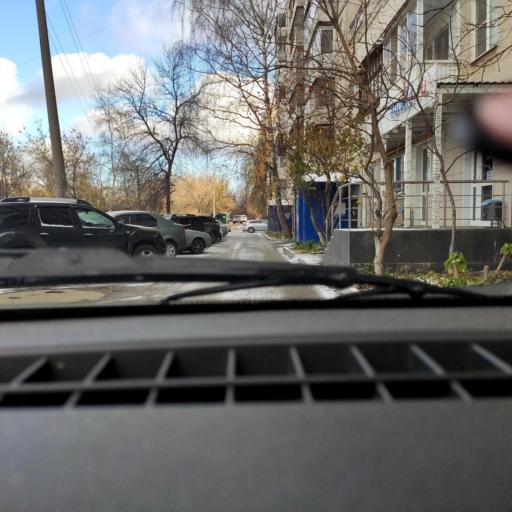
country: RU
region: Bashkortostan
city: Ufa
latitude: 54.7212
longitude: 56.0073
